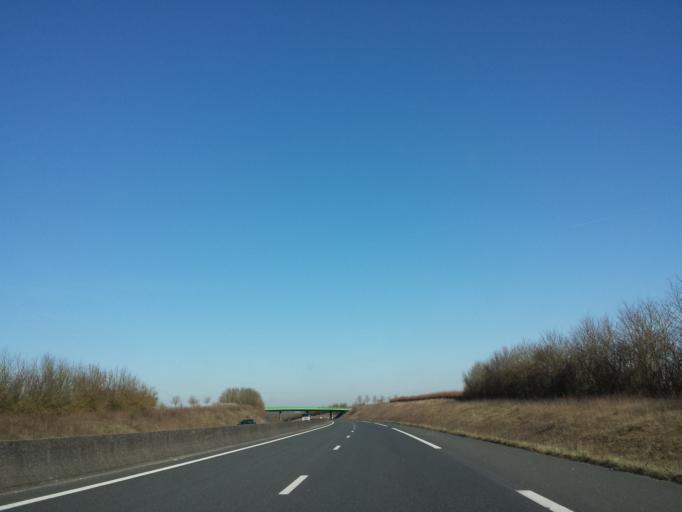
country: FR
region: Picardie
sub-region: Departement de l'Oise
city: Tille
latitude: 49.5195
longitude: 2.1864
